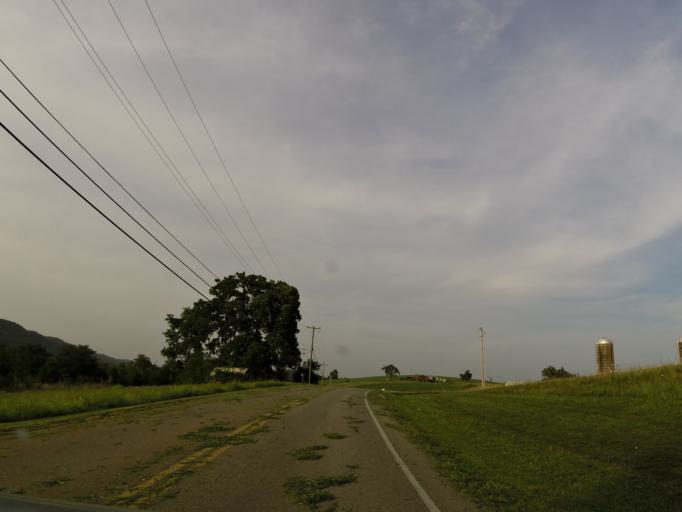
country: US
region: Tennessee
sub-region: Blount County
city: Wildwood
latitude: 35.8354
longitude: -83.8456
